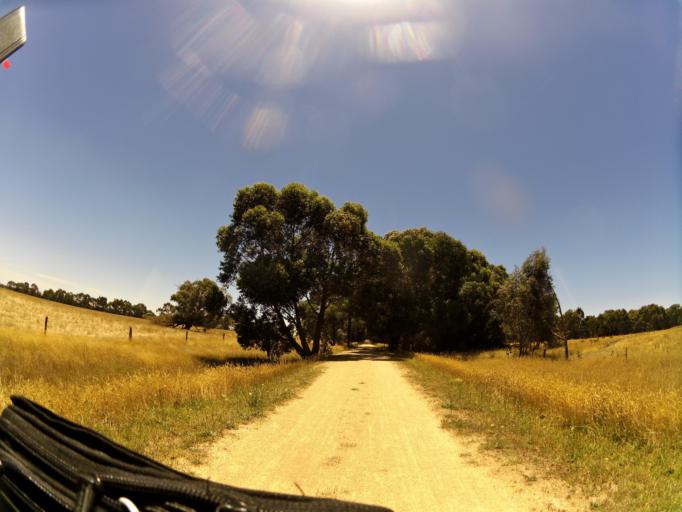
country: AU
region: Victoria
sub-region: Ballarat North
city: Delacombe
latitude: -37.5748
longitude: 143.7284
